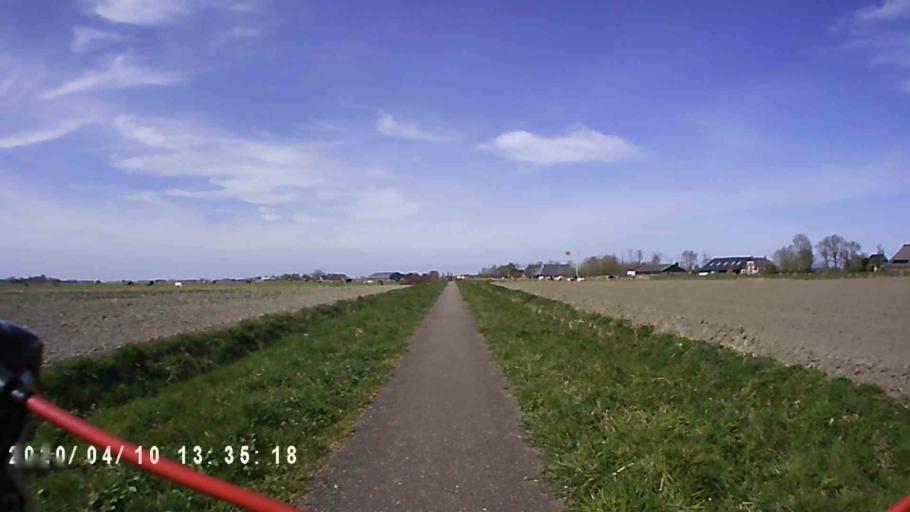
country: NL
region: Groningen
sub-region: Gemeente Zuidhorn
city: Oldehove
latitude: 53.3699
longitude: 6.4023
